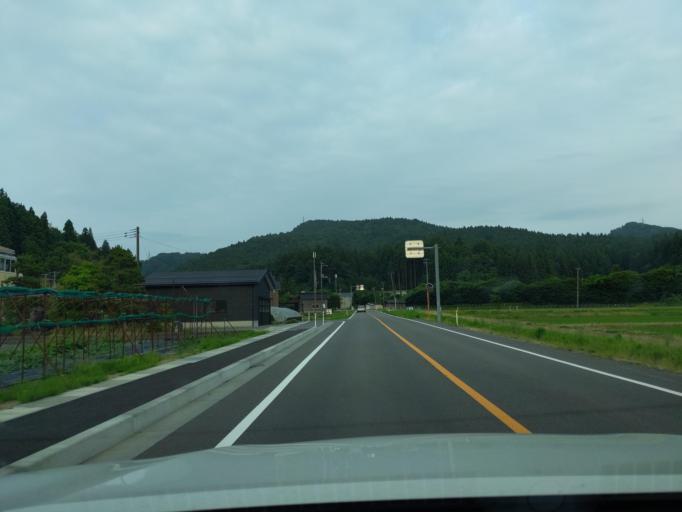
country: JP
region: Niigata
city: Kashiwazaki
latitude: 37.4472
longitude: 138.6663
